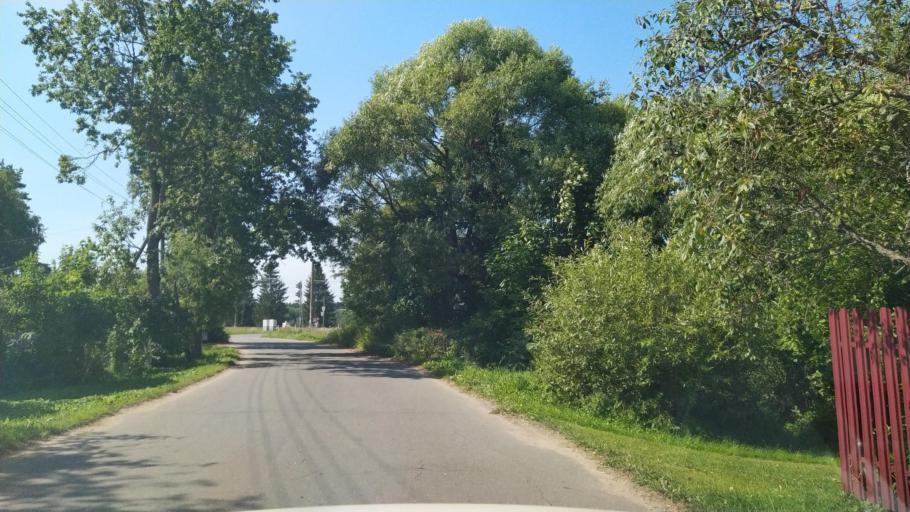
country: RU
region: Leningrad
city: Rozhdestveno
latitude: 59.2625
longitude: 30.0318
